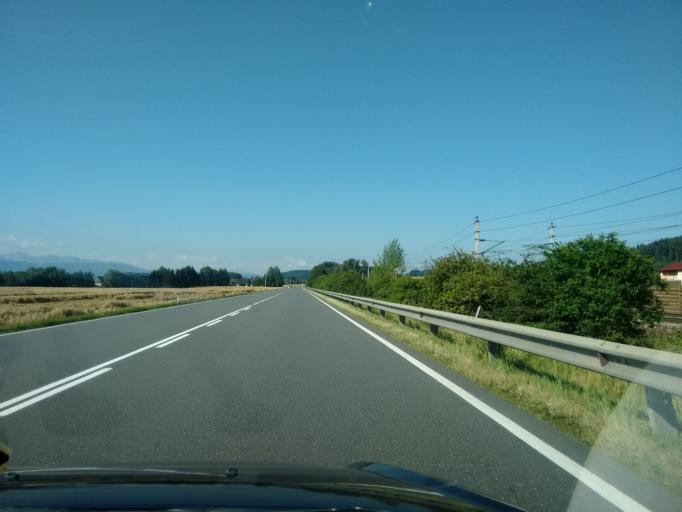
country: AT
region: Upper Austria
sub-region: Politischer Bezirk Vocklabruck
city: Oberndorf bei Schwanenstadt
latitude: 48.0426
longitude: 13.7513
